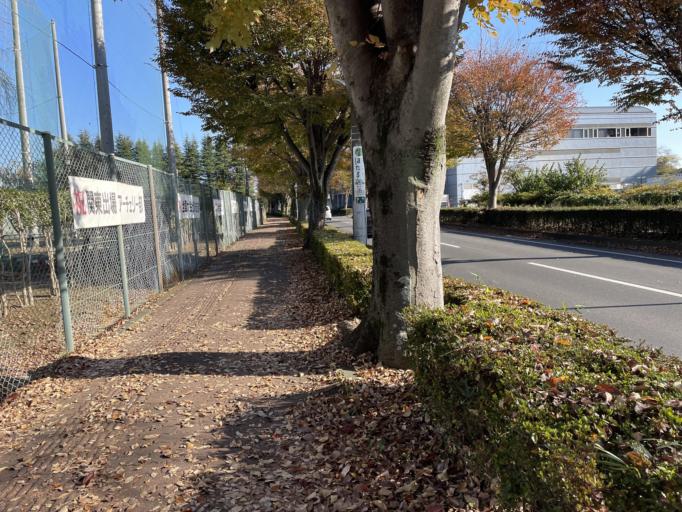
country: JP
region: Gunma
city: Tatebayashi
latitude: 36.2448
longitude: 139.5440
